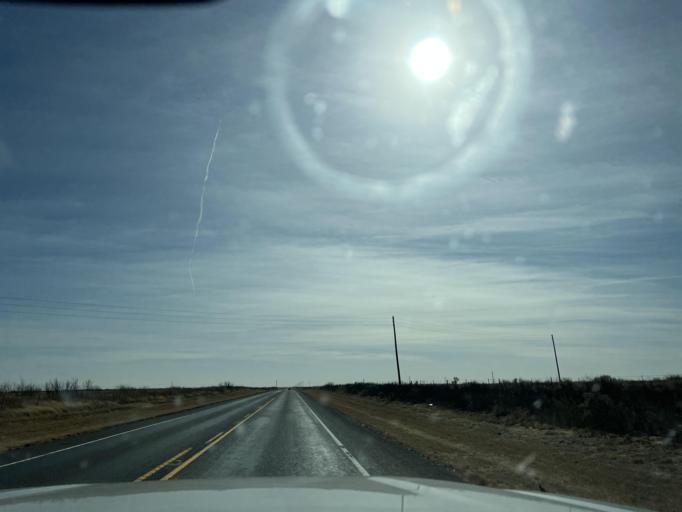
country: US
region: Texas
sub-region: Andrews County
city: Andrews
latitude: 32.4297
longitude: -102.4373
